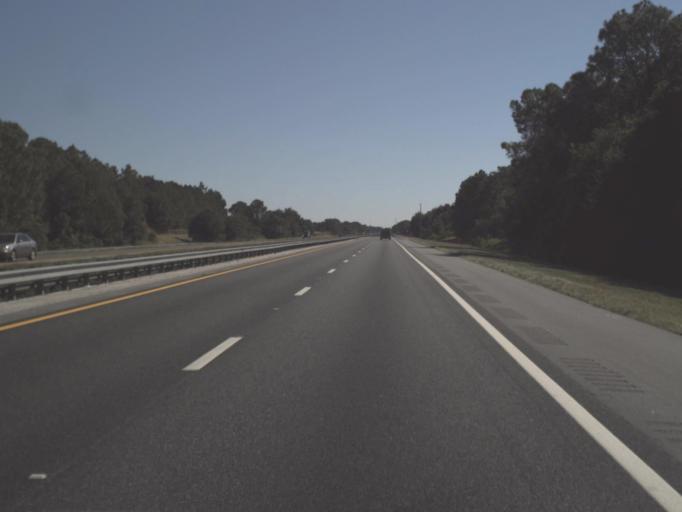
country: US
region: Florida
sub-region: Lake County
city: Howie In The Hills
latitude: 28.6609
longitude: -81.8252
